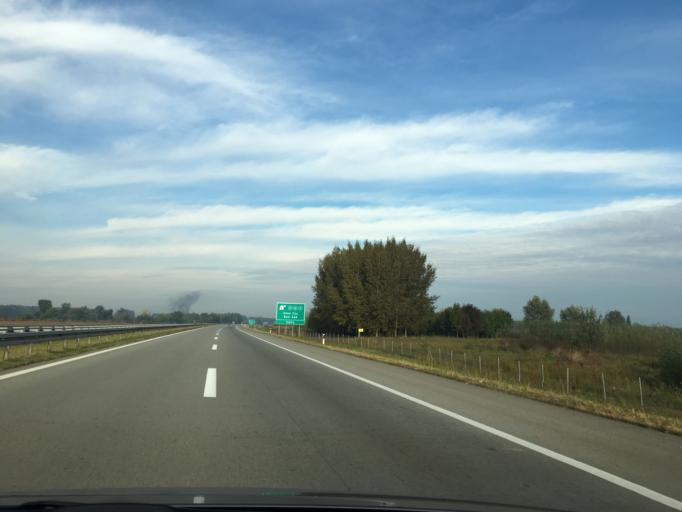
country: RS
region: Autonomna Pokrajina Vojvodina
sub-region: Juznobacki Okrug
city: Petrovaradin
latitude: 45.2782
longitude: 19.9143
